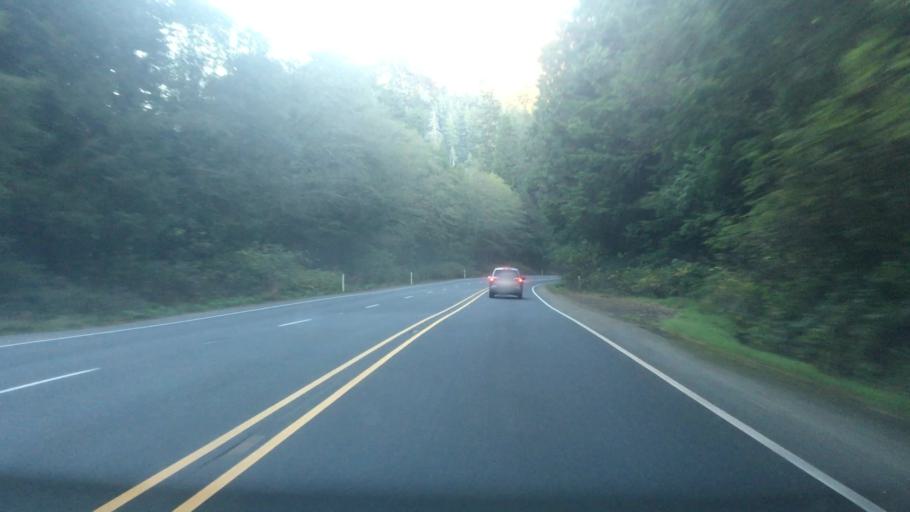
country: US
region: Oregon
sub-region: Clatsop County
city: Cannon Beach
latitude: 45.7766
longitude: -123.9477
